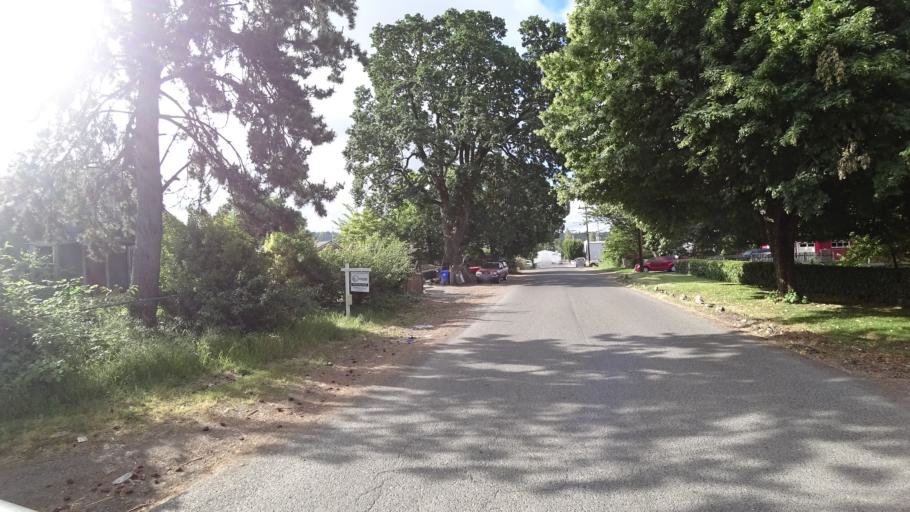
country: US
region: Oregon
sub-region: Multnomah County
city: Lents
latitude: 45.4783
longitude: -122.5574
